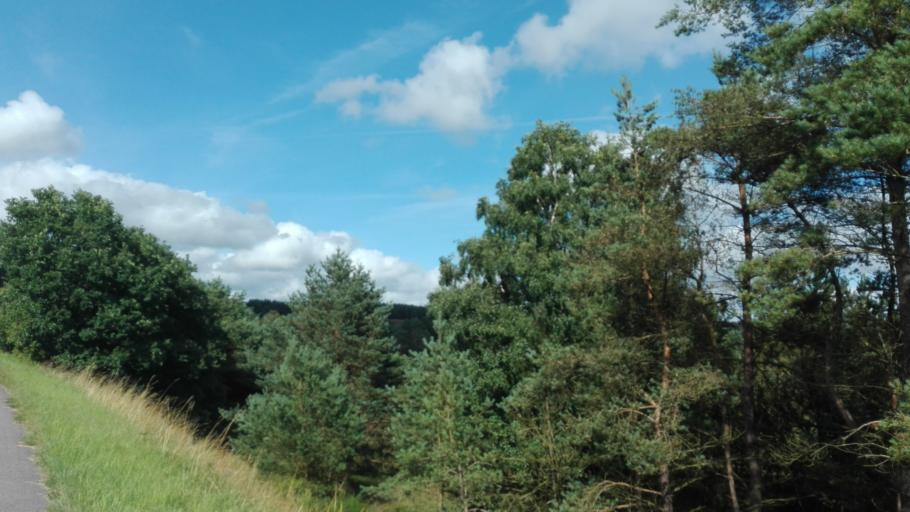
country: DK
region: Central Jutland
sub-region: Silkeborg Kommune
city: Virklund
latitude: 56.0513
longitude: 9.4716
